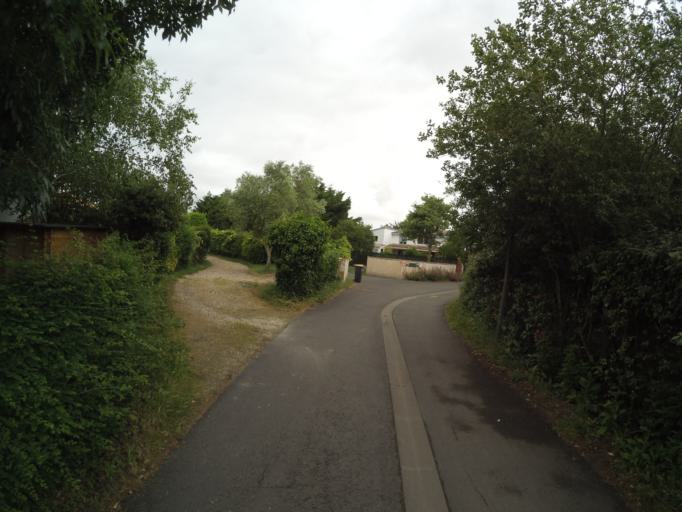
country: FR
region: Poitou-Charentes
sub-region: Departement de la Charente-Maritime
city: Aytre
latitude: 46.1285
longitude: -1.1281
